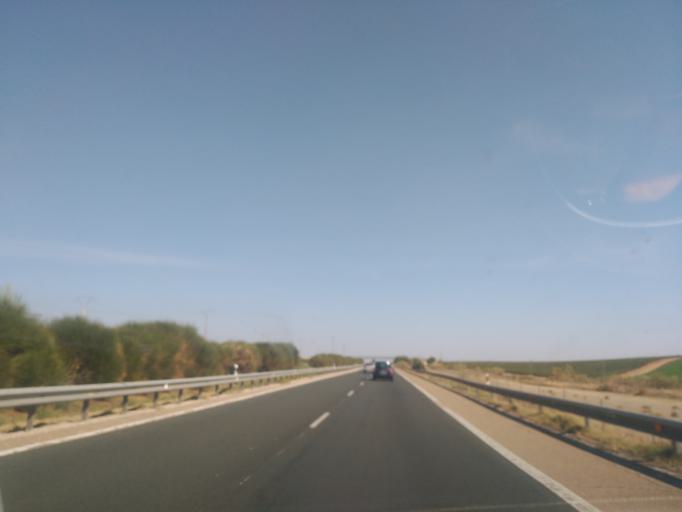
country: ES
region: Castille and Leon
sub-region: Provincia de Valladolid
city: Cisterniga
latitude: 41.5969
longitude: -4.6413
